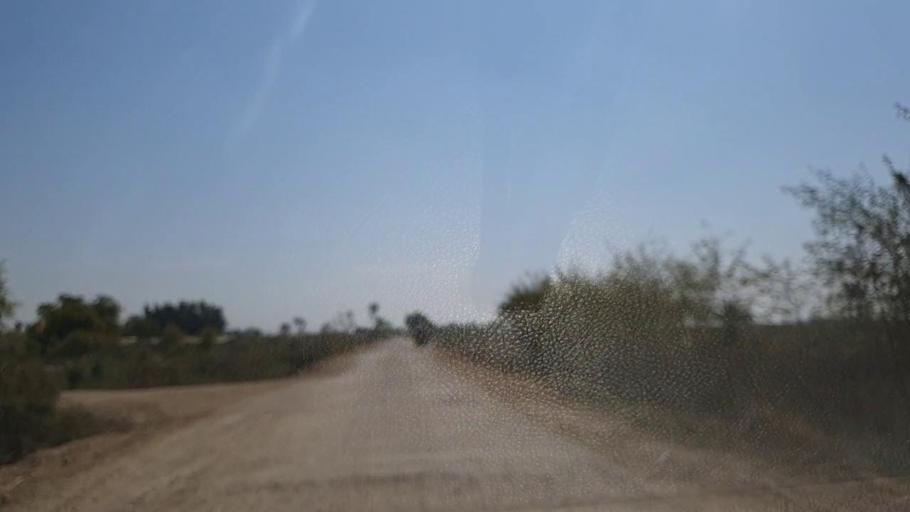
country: PK
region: Sindh
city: Samaro
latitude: 25.3811
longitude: 69.3310
